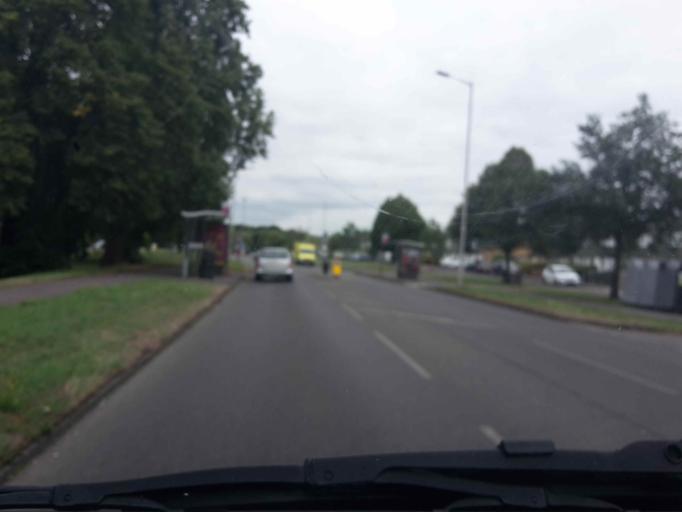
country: GB
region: England
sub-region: Reading
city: Reading
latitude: 51.4789
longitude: -0.9654
